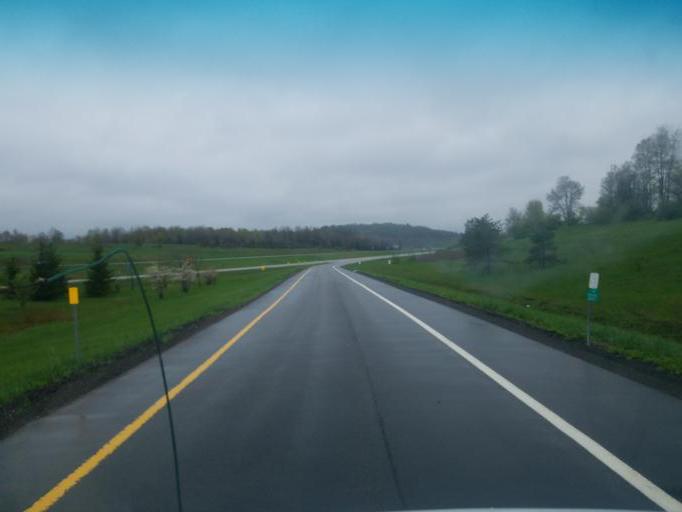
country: US
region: New York
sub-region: Chautauqua County
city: Mayville
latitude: 42.1529
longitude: -79.5955
